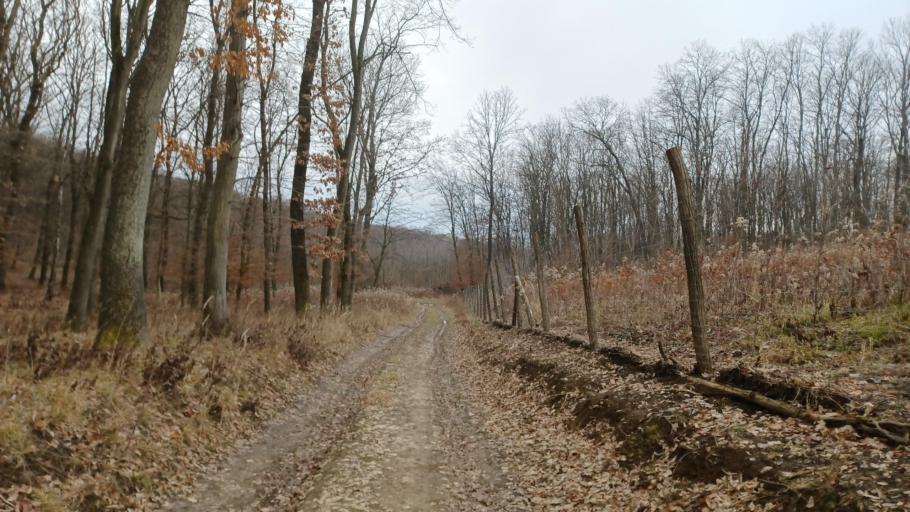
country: HU
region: Tolna
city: Szentgalpuszta
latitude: 46.3049
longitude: 18.6402
